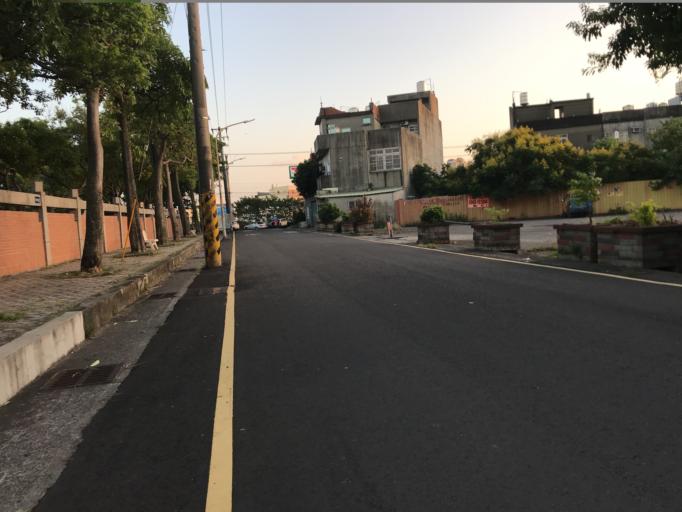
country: TW
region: Taiwan
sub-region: Hsinchu
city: Hsinchu
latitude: 24.8058
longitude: 120.9403
